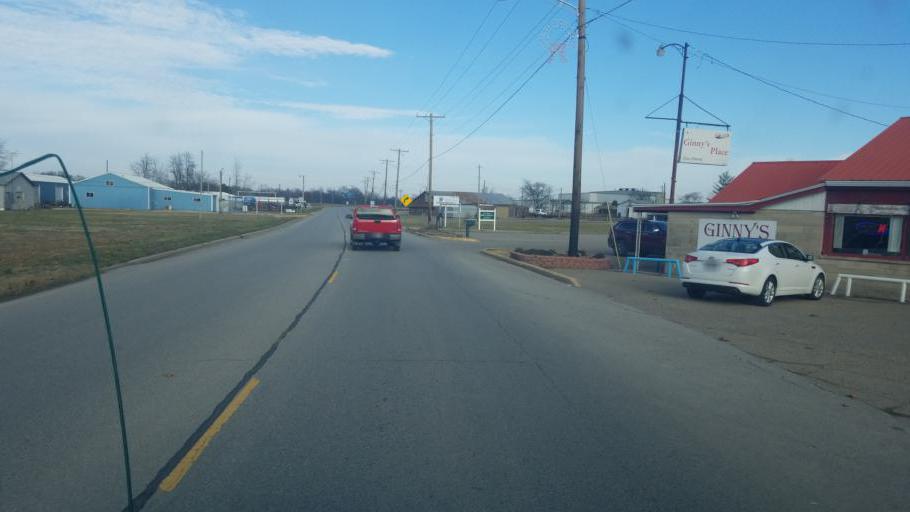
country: US
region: Illinois
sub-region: White County
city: Carmi
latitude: 38.0978
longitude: -88.1462
